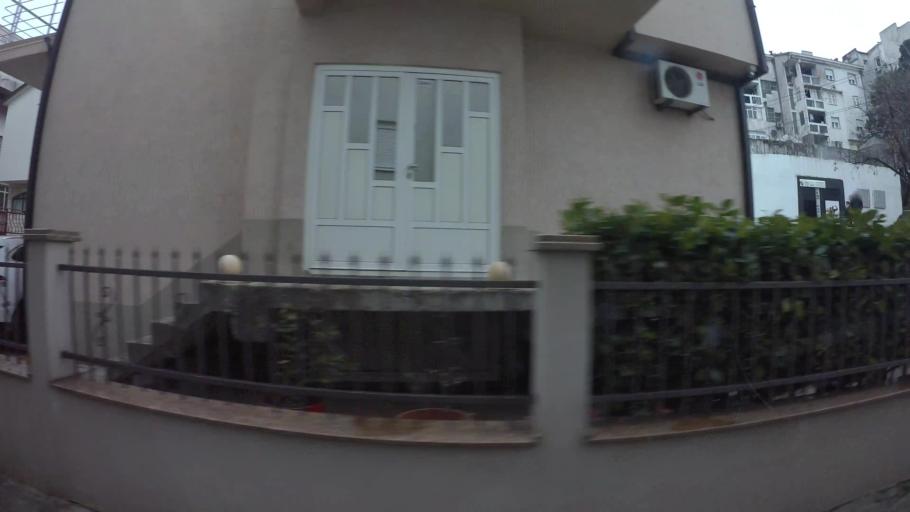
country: BA
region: Federation of Bosnia and Herzegovina
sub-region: Hercegovacko-Bosanski Kanton
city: Mostar
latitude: 43.3568
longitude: 17.8150
